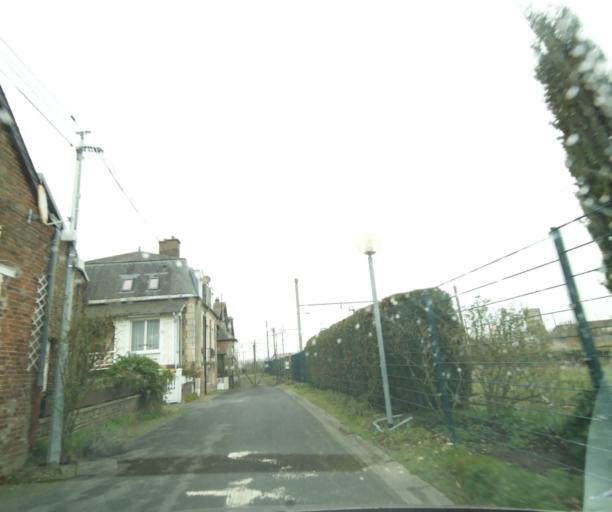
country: FR
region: Picardie
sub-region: Departement de l'Oise
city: Noyon
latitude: 49.5779
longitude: 3.0117
